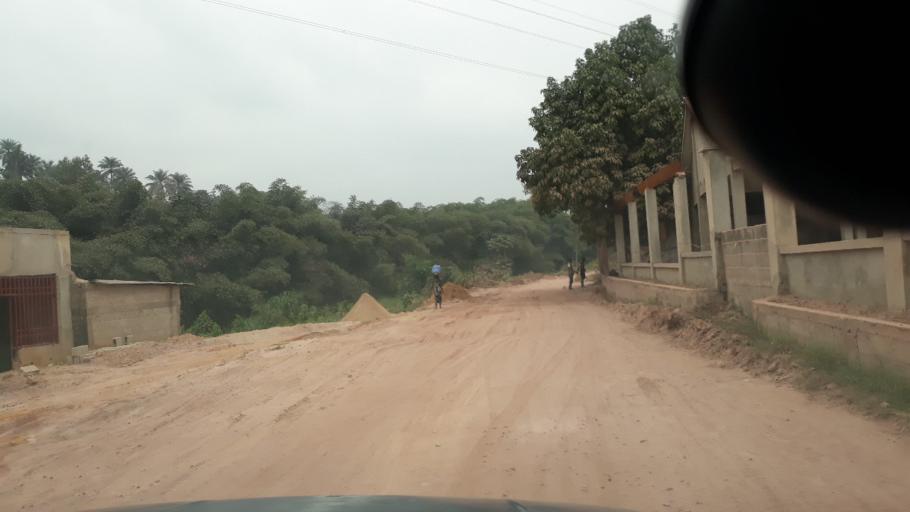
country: CD
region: Kinshasa
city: Masina
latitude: -4.4773
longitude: 15.2756
